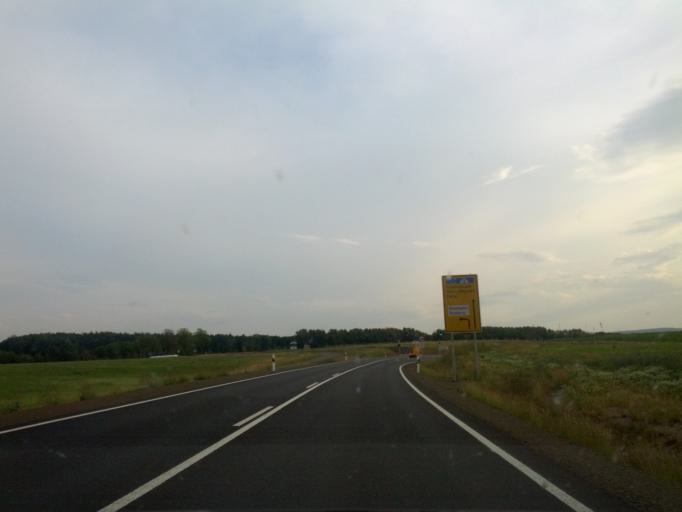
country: DE
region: Thuringia
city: Emleben
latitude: 50.9174
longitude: 10.6523
